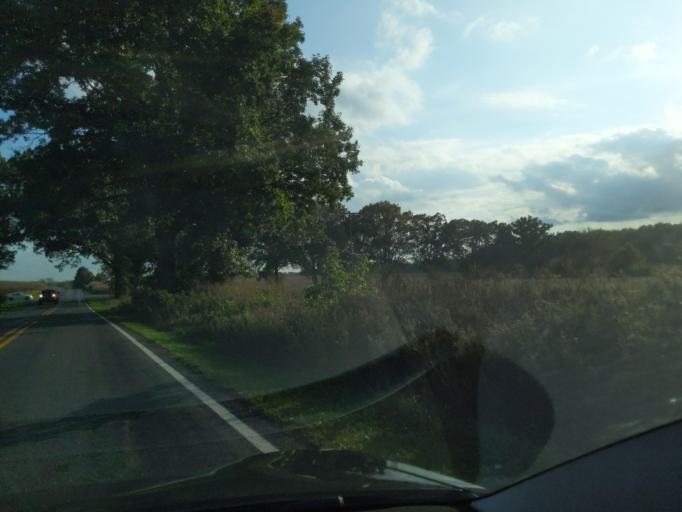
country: US
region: Michigan
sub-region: Ingham County
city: Leslie
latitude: 42.3506
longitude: -84.4629
